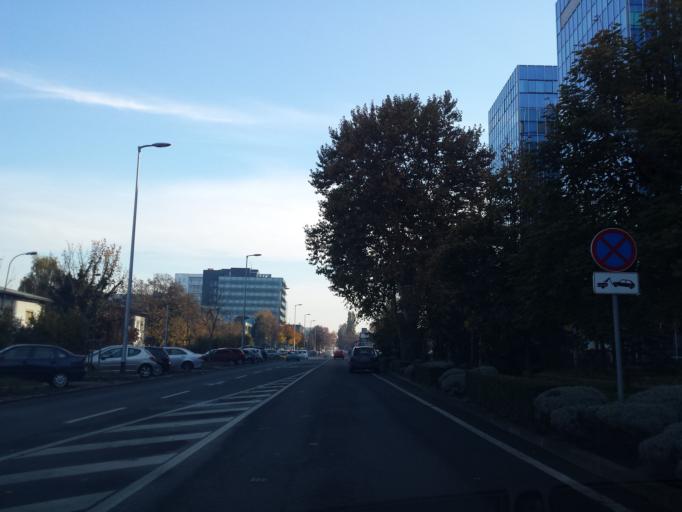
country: HR
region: Grad Zagreb
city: Zagreb - Centar
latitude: 45.8036
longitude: 16.0000
